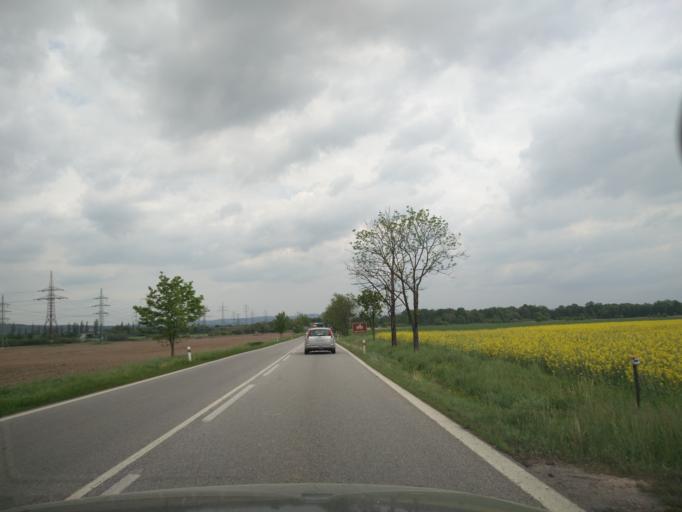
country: CZ
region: Jihocesky
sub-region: Okres Ceske Budejovice
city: Hluboka nad Vltavou
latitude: 49.0173
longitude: 14.4244
